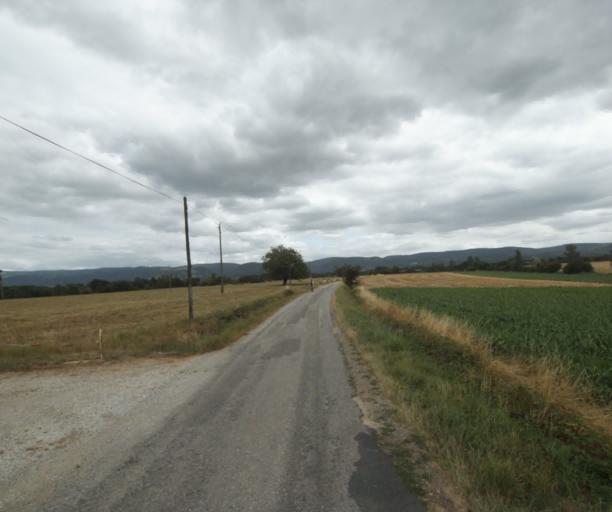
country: FR
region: Midi-Pyrenees
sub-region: Departement de la Haute-Garonne
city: Revel
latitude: 43.4835
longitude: 2.0290
